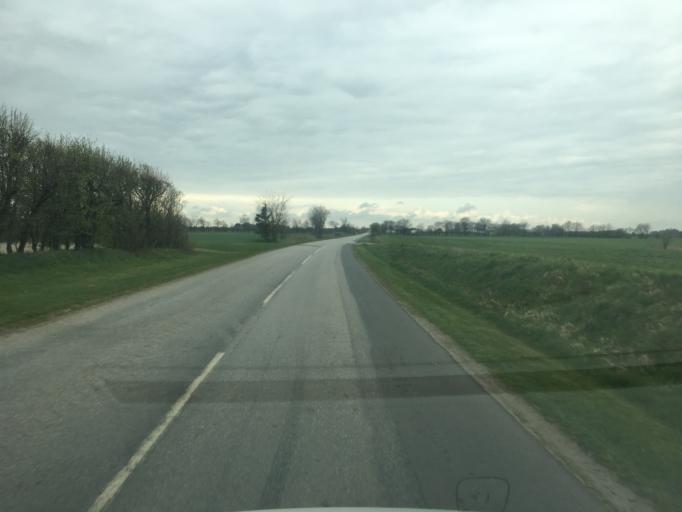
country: DK
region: South Denmark
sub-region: Aabenraa Kommune
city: Tinglev
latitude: 55.0269
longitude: 9.1629
